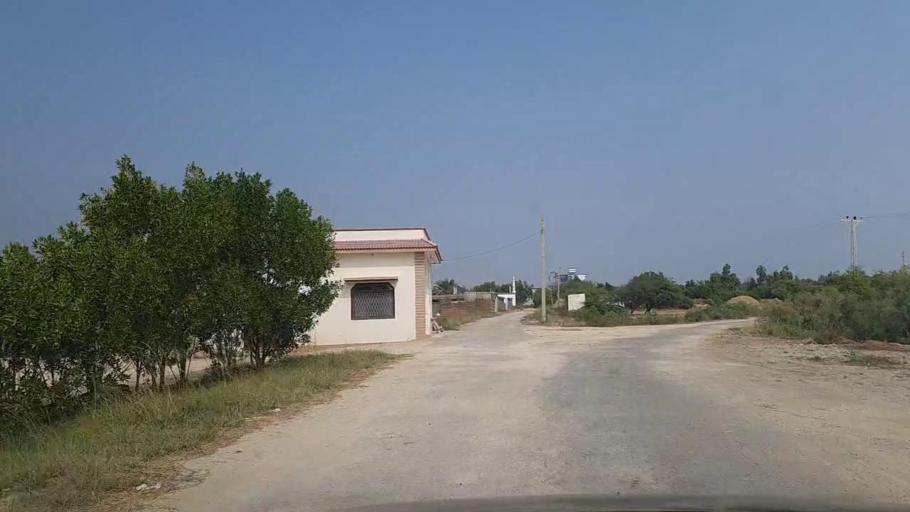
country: PK
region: Sindh
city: Thatta
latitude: 24.7454
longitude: 67.7959
